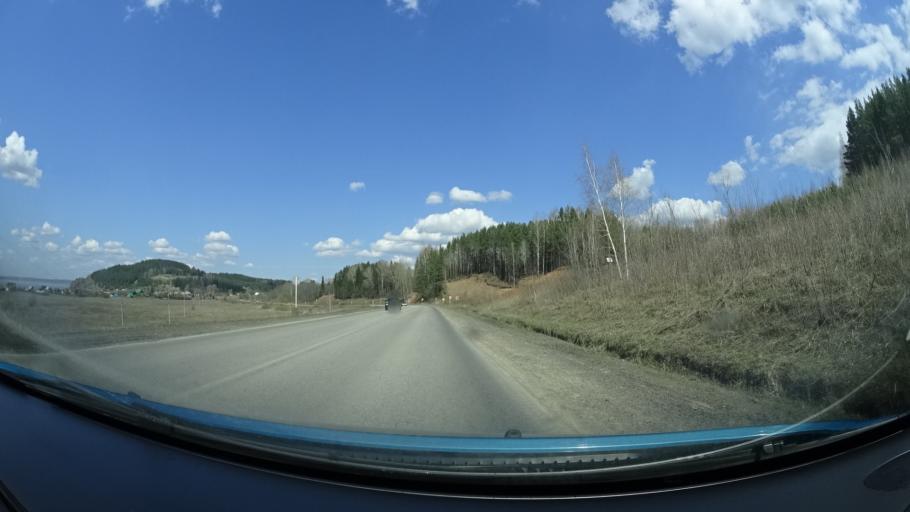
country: RU
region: Perm
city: Osa
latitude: 57.2164
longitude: 55.5918
